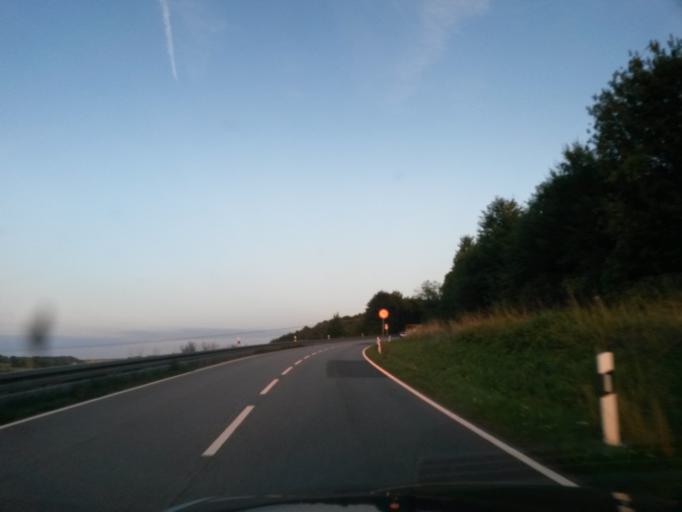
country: DE
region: Bavaria
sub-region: Regierungsbezirk Unterfranken
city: Marktheidenfeld
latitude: 49.8131
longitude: 9.6405
